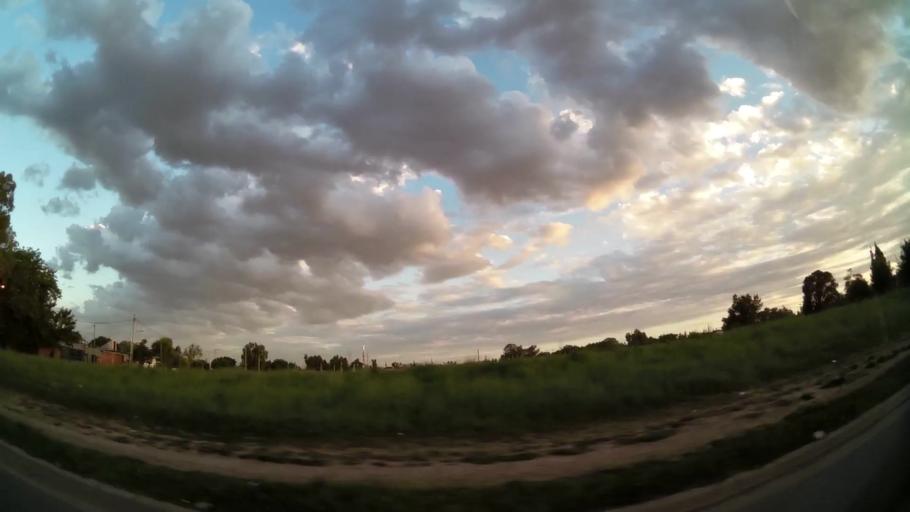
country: AR
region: Buenos Aires
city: Santa Catalina - Dique Lujan
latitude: -34.4882
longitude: -58.7516
